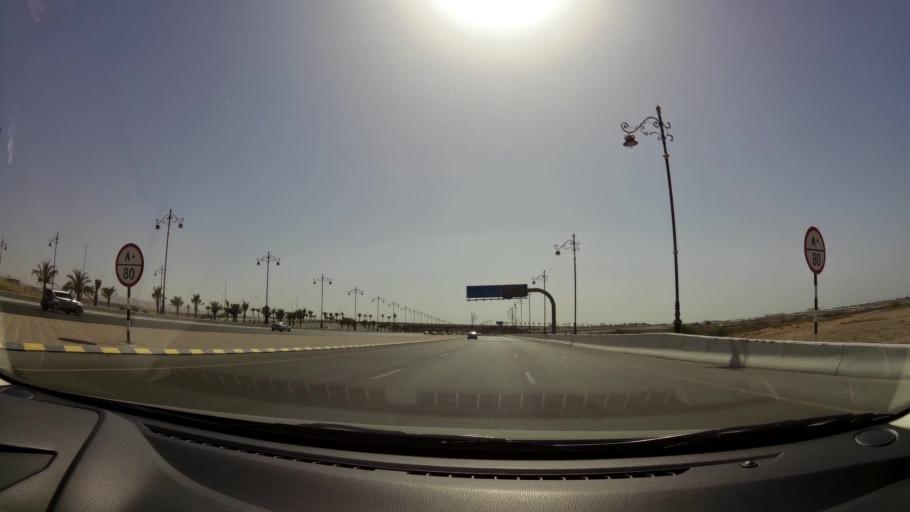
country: OM
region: Muhafazat Masqat
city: Bawshar
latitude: 23.5929
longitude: 58.3426
